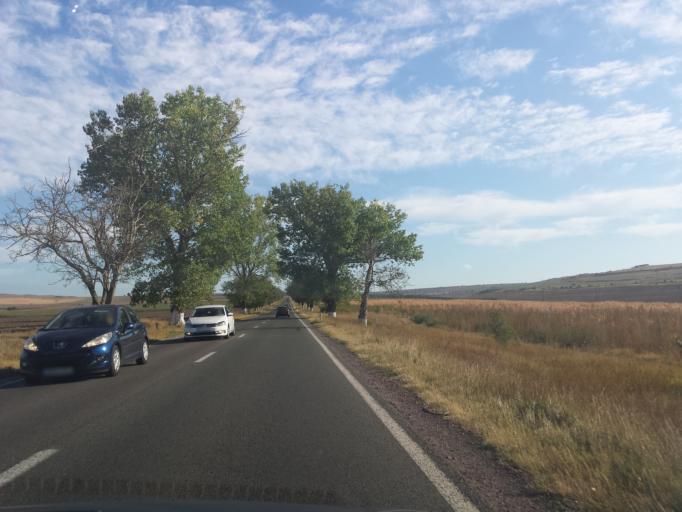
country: RO
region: Tulcea
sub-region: Comuna Frecatei
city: Cataloi
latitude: 45.1066
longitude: 28.7438
